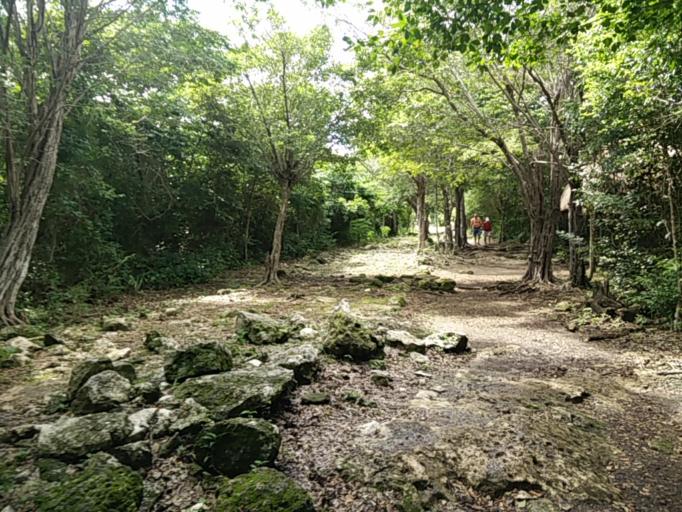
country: MX
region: Quintana Roo
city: San Miguel de Cozumel
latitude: 20.5017
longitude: -86.8443
